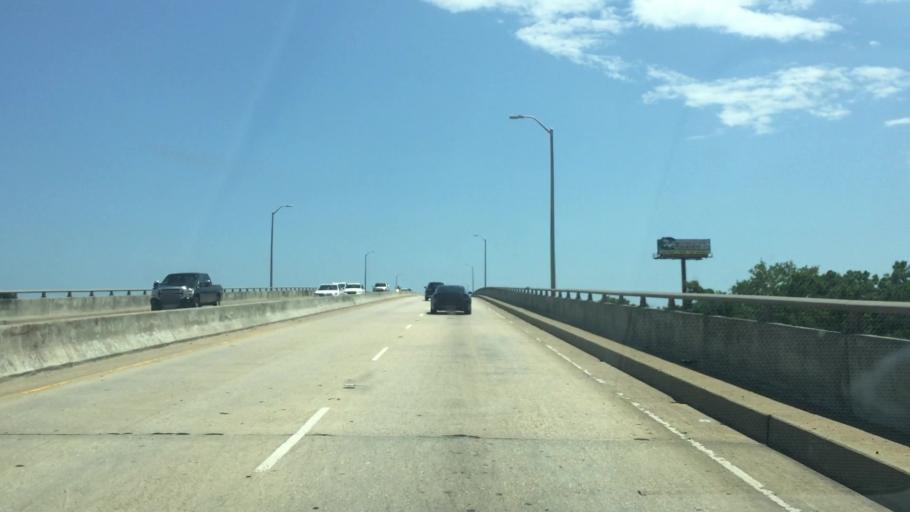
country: US
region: South Carolina
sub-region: Horry County
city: Little River
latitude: 33.8553
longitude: -78.6551
